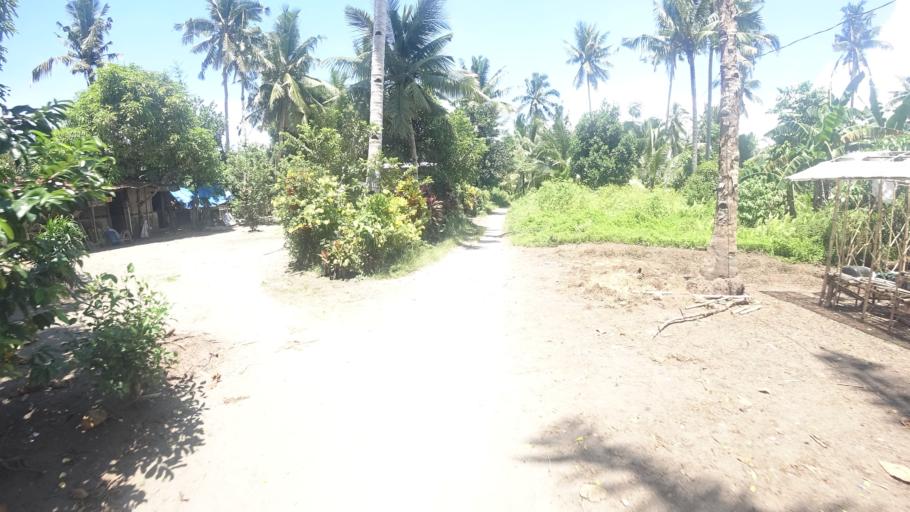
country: PH
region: Eastern Visayas
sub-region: Province of Leyte
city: Mayorga
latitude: 10.8892
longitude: 125.0067
